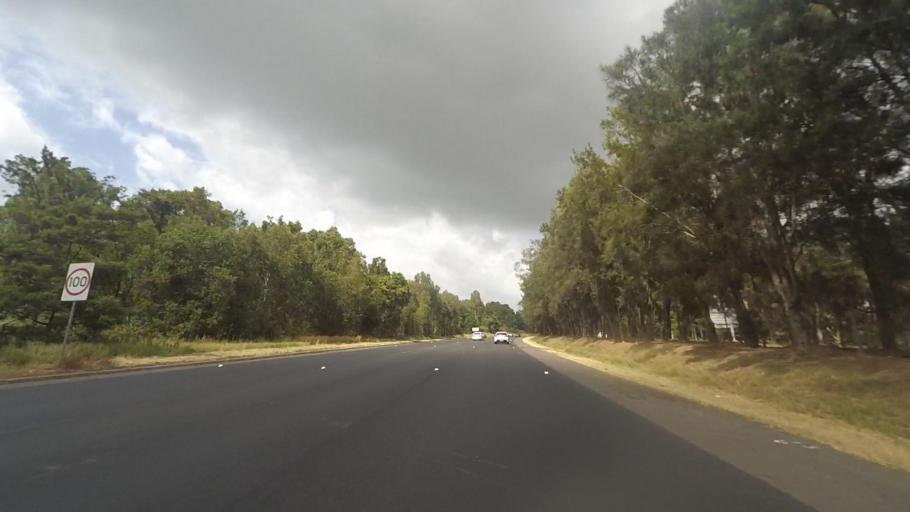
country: AU
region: New South Wales
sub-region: Wollongong
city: Berkeley
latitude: -34.4629
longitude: 150.8515
